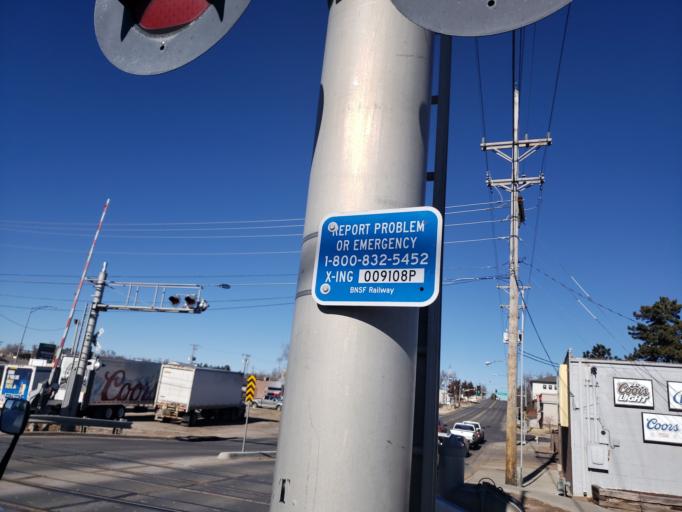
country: US
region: Kansas
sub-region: Ford County
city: Dodge City
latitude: 37.7530
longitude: -100.0329
